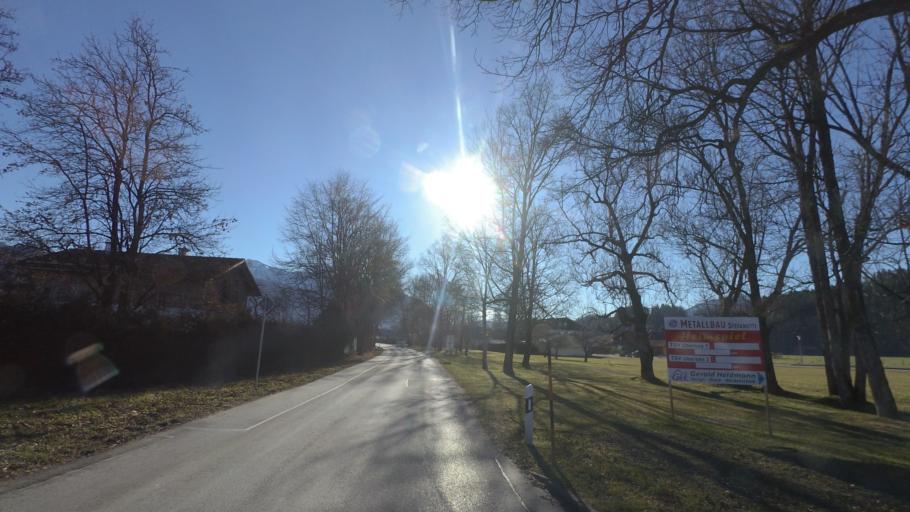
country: DE
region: Bavaria
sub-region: Upper Bavaria
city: Ubersee
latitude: 47.8118
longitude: 12.4804
